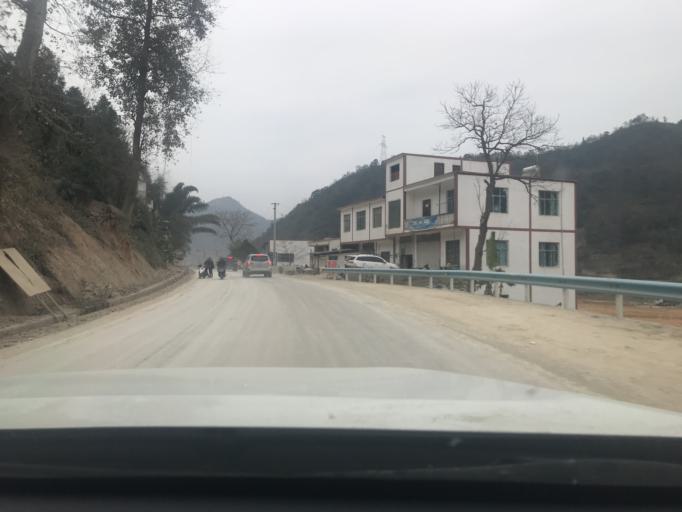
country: CN
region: Guangxi Zhuangzu Zizhiqu
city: Xinzhou
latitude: 25.0103
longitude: 105.8472
